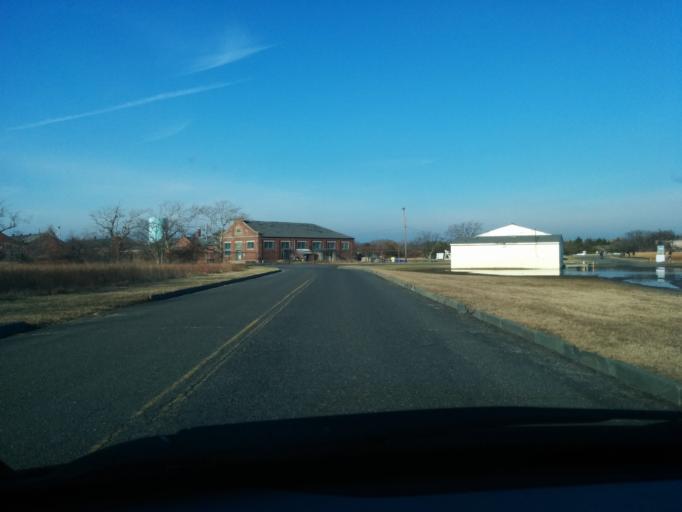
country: US
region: New Jersey
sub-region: Monmouth County
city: Highlands
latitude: 40.4686
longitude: -74.0028
